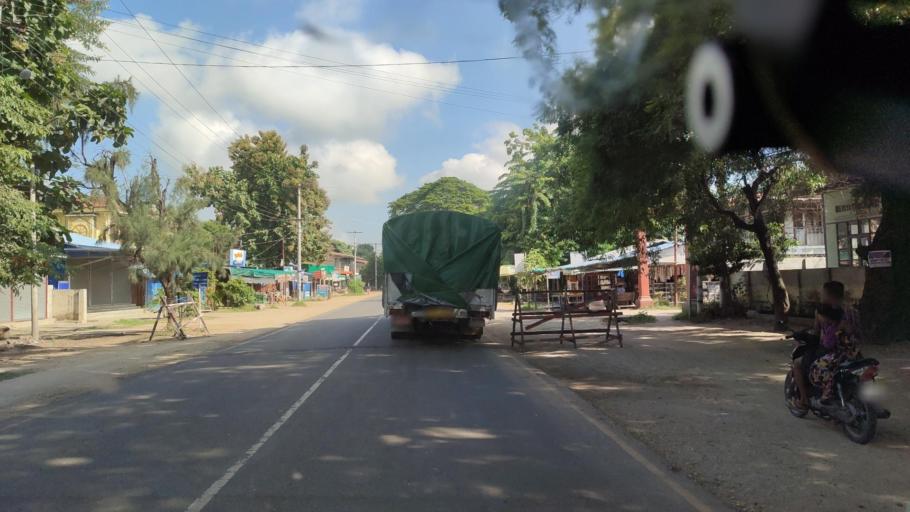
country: MM
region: Sagain
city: Shwebo
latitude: 22.5609
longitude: 96.0660
